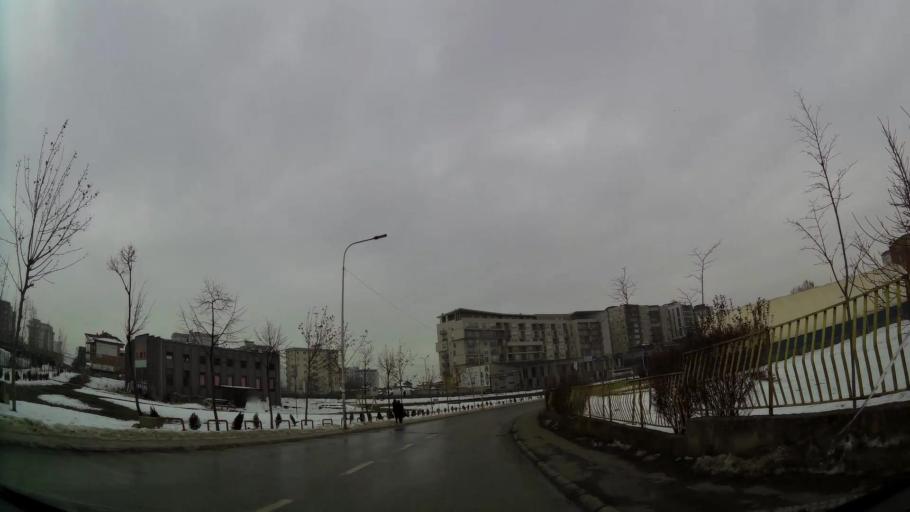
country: XK
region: Pristina
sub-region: Komuna e Prishtines
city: Pristina
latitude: 42.6492
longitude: 21.1542
